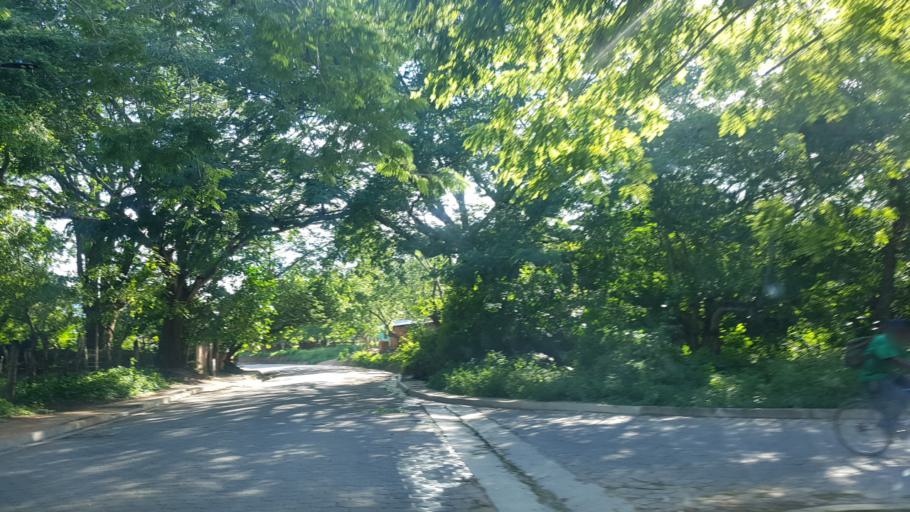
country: NI
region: Nueva Segovia
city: Mozonte
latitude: 13.6572
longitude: -86.4397
